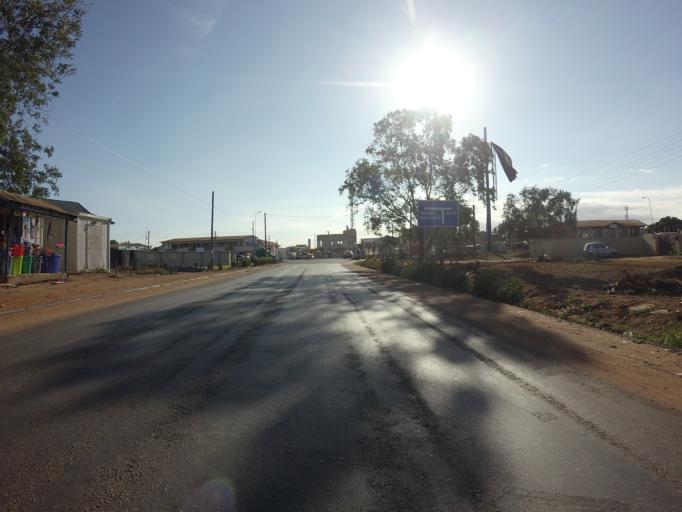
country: GH
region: Greater Accra
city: Nungua
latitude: 5.6487
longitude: -0.0756
